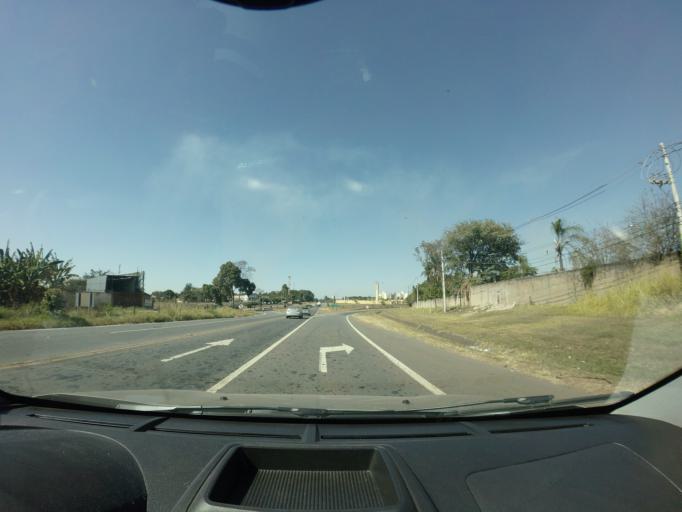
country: BR
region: Sao Paulo
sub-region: Piracicaba
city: Piracicaba
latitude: -22.7355
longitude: -47.6040
